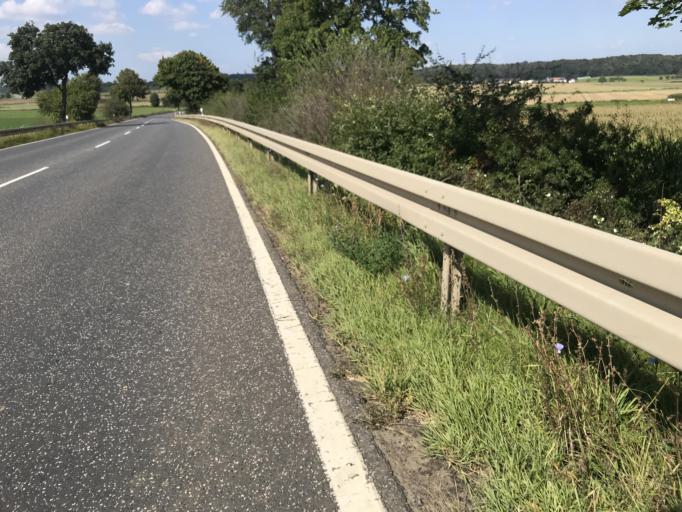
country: DE
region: Hesse
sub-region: Regierungsbezirk Giessen
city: Hungen
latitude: 50.4575
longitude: 8.9382
